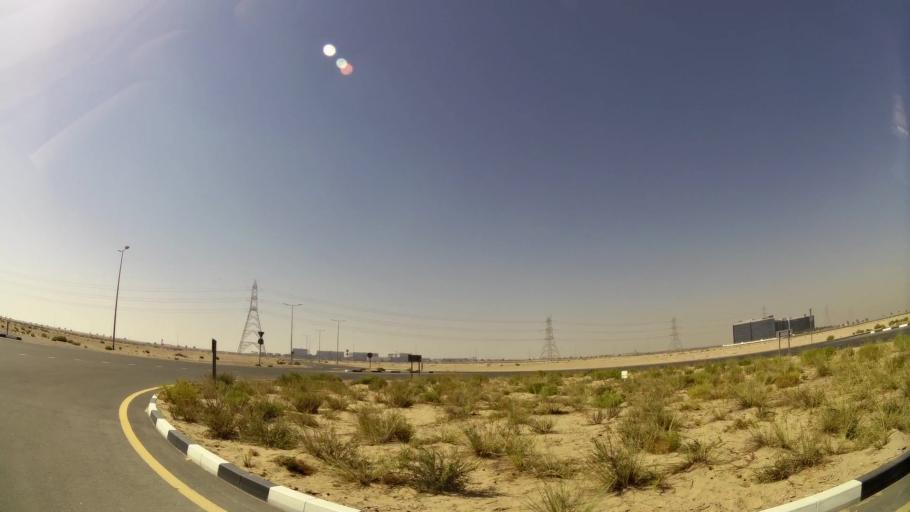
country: AE
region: Dubai
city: Dubai
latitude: 24.9037
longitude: 55.0652
